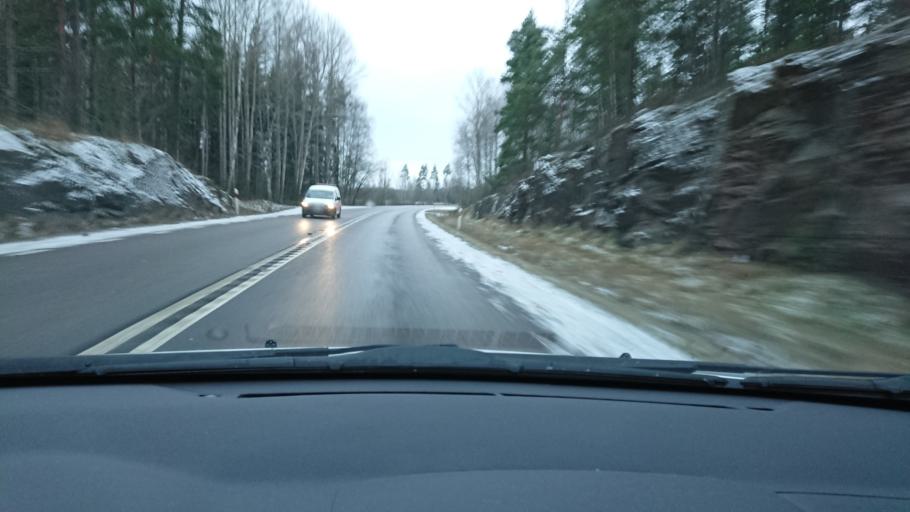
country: SE
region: Kalmar
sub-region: Hultsfreds Kommun
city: Hultsfred
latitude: 57.4959
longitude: 15.8210
